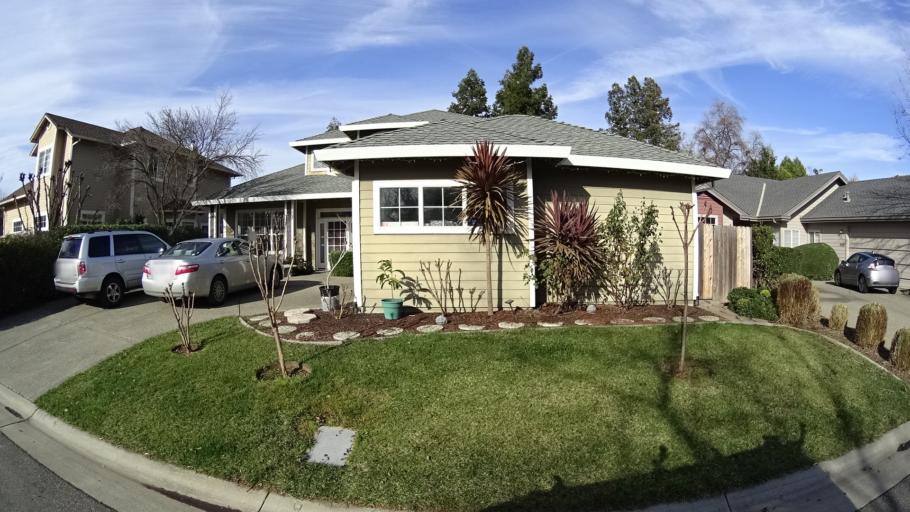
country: US
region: California
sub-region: Yolo County
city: Davis
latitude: 38.5447
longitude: -121.7014
